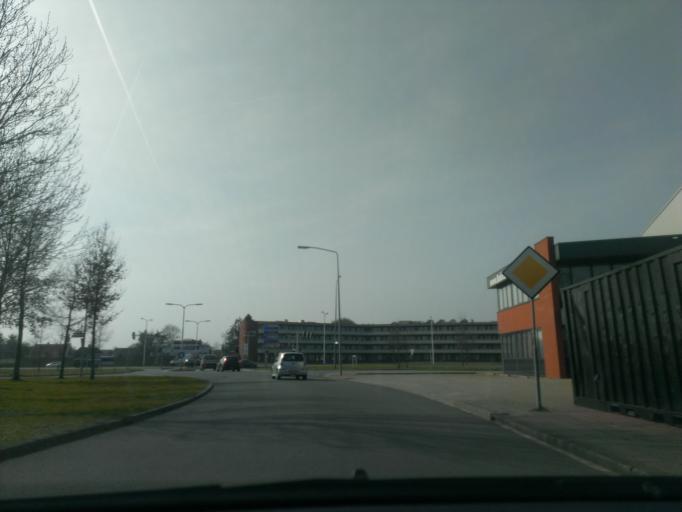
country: NL
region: Overijssel
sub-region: Gemeente Almelo
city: Almelo
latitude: 52.3414
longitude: 6.6824
